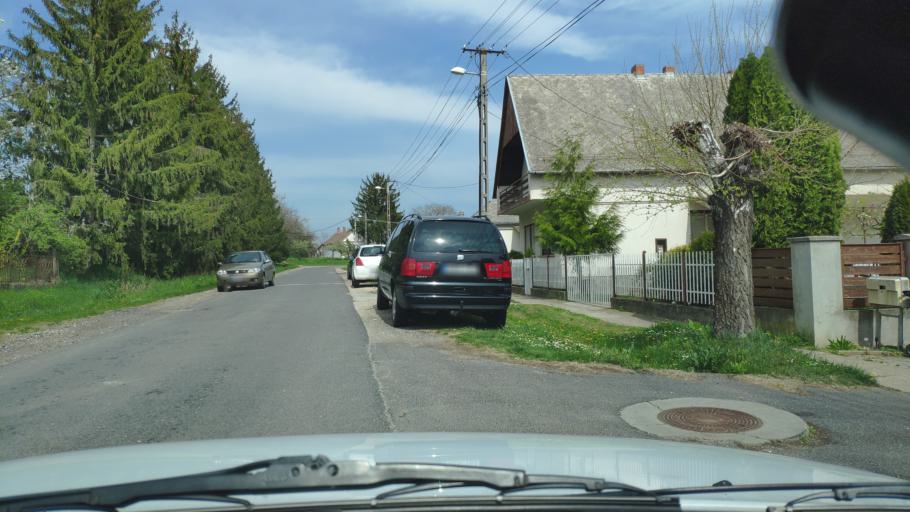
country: HU
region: Zala
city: Nagykanizsa
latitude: 46.4170
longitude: 16.9898
